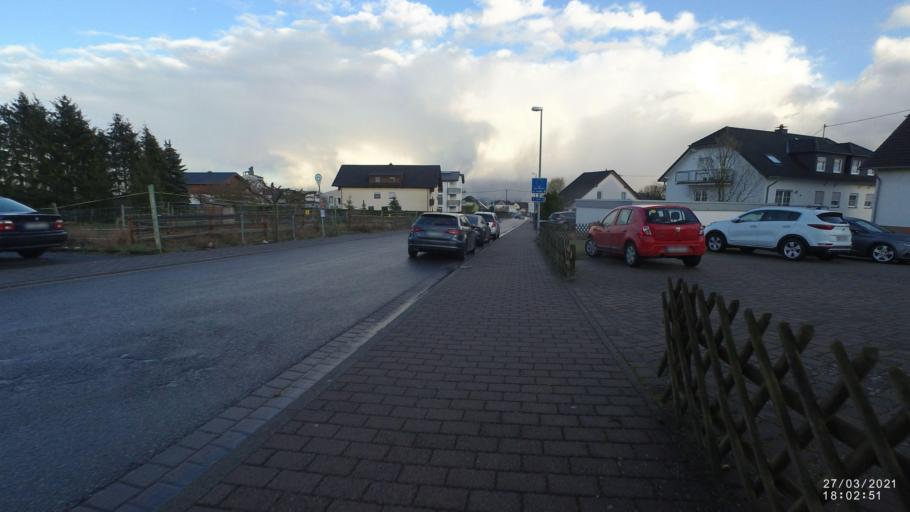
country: DE
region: Rheinland-Pfalz
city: Bell
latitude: 50.3770
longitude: 7.2560
